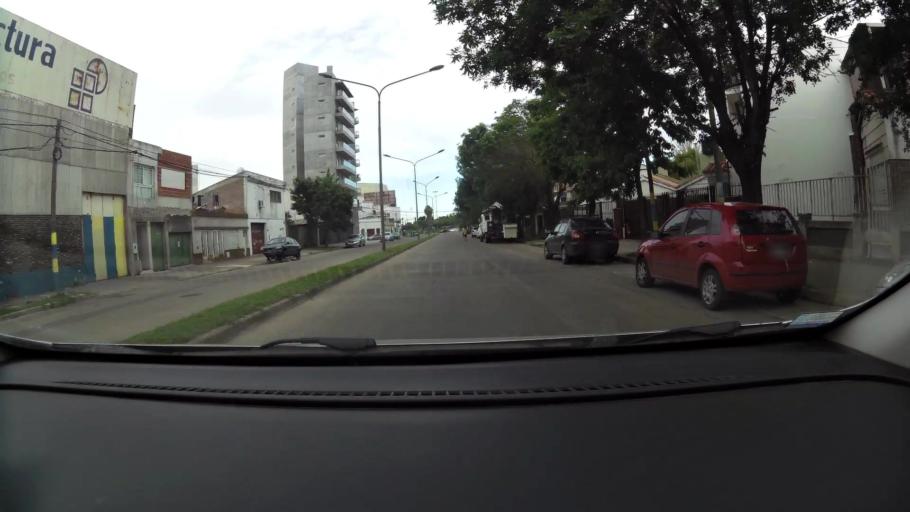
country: AR
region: Santa Fe
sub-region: Departamento de Rosario
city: Rosario
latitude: -32.9137
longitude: -60.6854
